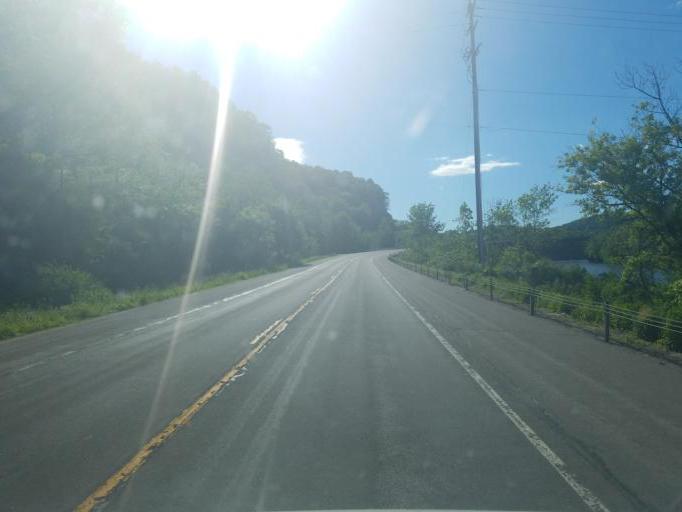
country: US
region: New York
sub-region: Herkimer County
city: Little Falls
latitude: 43.0361
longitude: -74.8406
